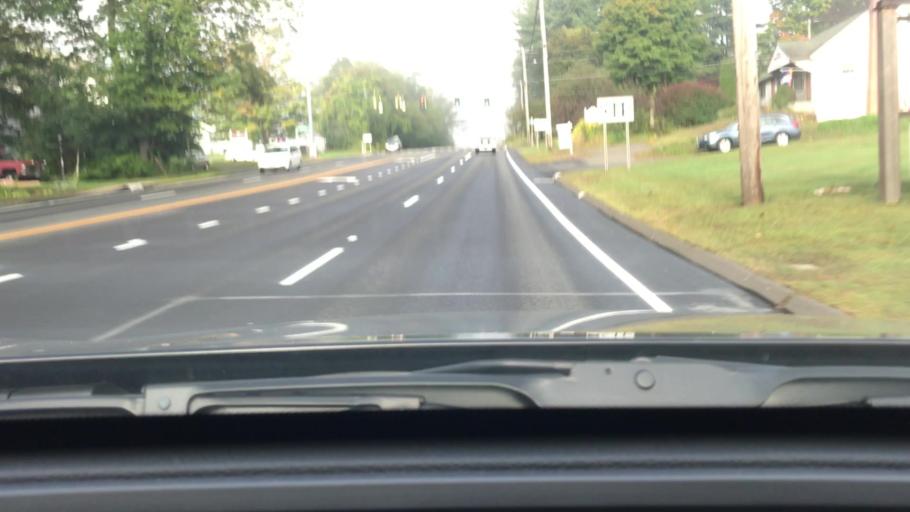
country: US
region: Connecticut
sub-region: Hartford County
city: Canton Valley
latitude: 41.8312
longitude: -72.9076
